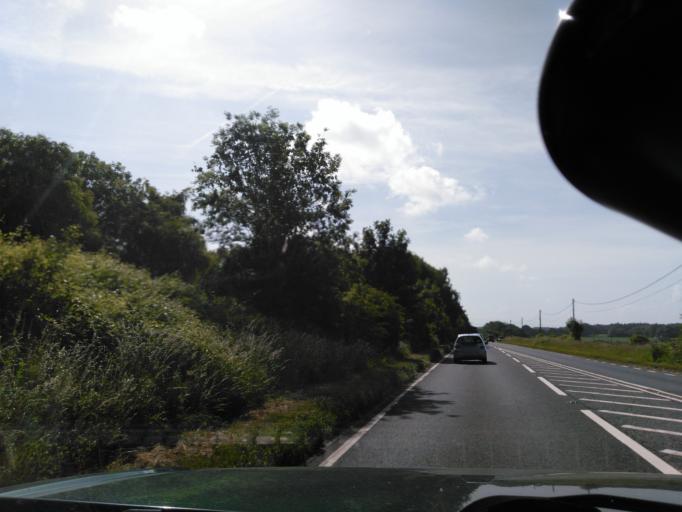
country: GB
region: England
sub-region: Wiltshire
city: Whiteparish
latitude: 51.0181
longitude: -1.6910
